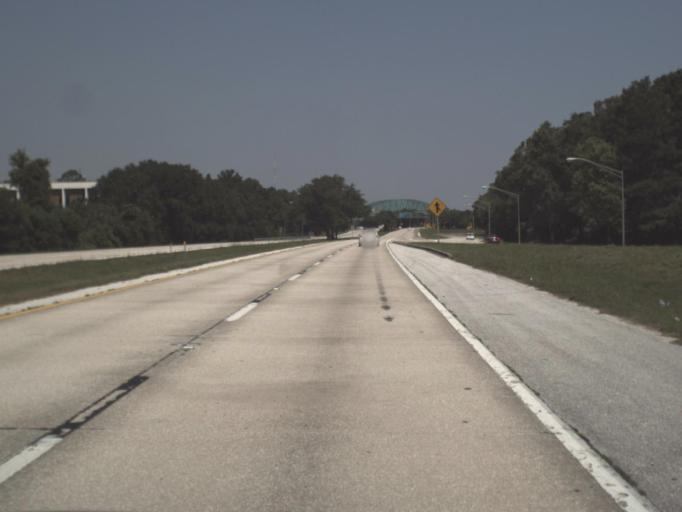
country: US
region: Florida
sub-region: Duval County
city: Jacksonville
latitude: 30.3043
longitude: -81.6144
